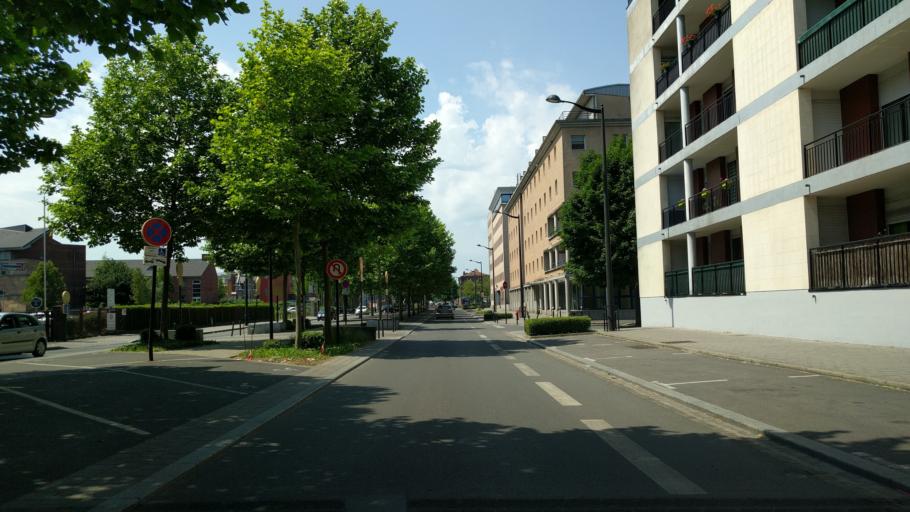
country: FR
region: Nord-Pas-de-Calais
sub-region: Departement du Nord
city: Valenciennes
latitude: 50.3642
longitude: 3.5259
